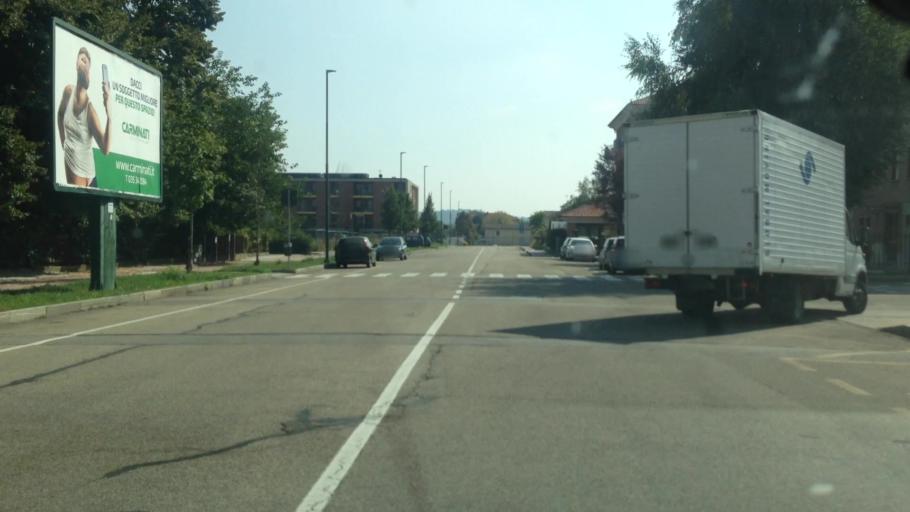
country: IT
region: Piedmont
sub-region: Provincia di Asti
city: Asti
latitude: 44.9027
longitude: 8.2217
